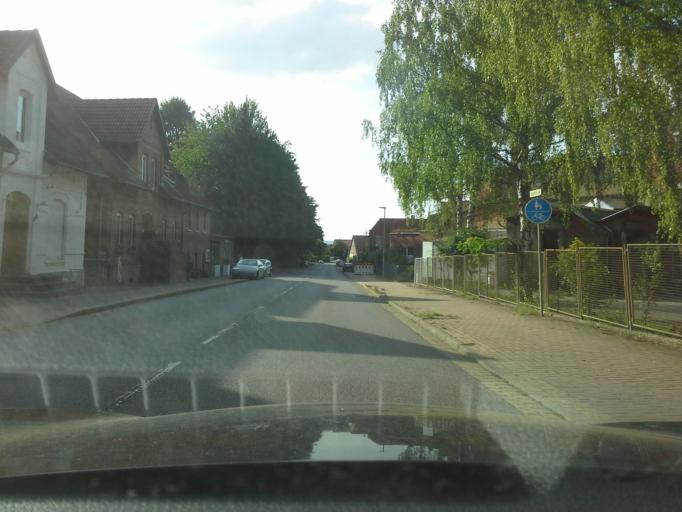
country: DE
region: Lower Saxony
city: Messenkamp
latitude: 52.2328
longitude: 9.4176
